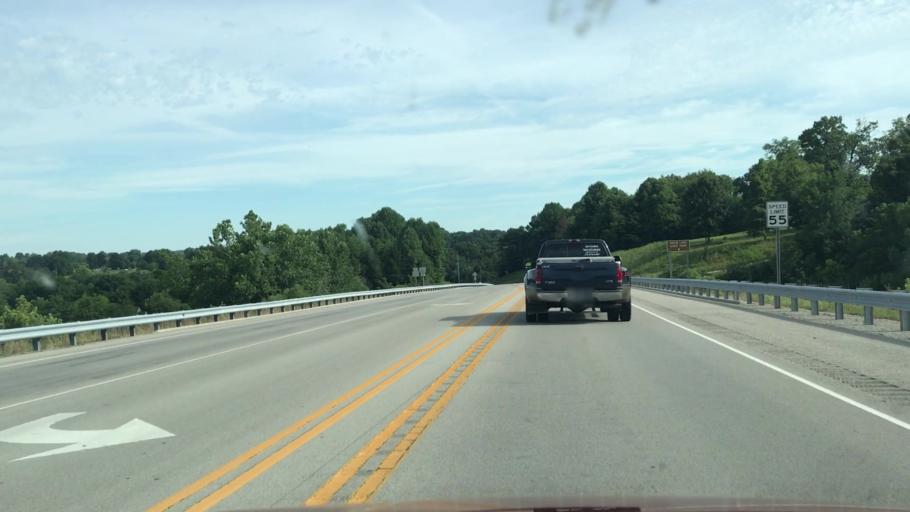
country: US
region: Kentucky
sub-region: Edmonson County
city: Brownsville
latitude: 37.1564
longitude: -86.2216
